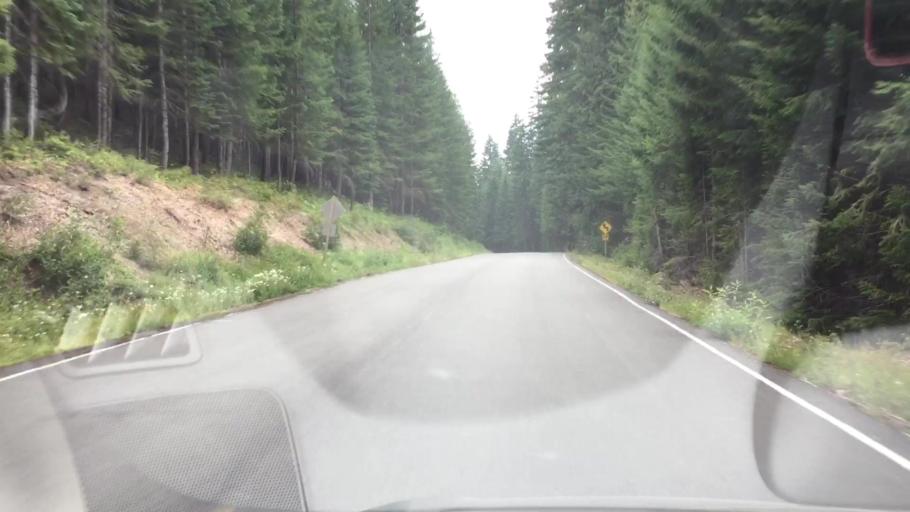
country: US
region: Washington
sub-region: Klickitat County
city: White Salmon
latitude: 46.2270
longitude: -121.6223
